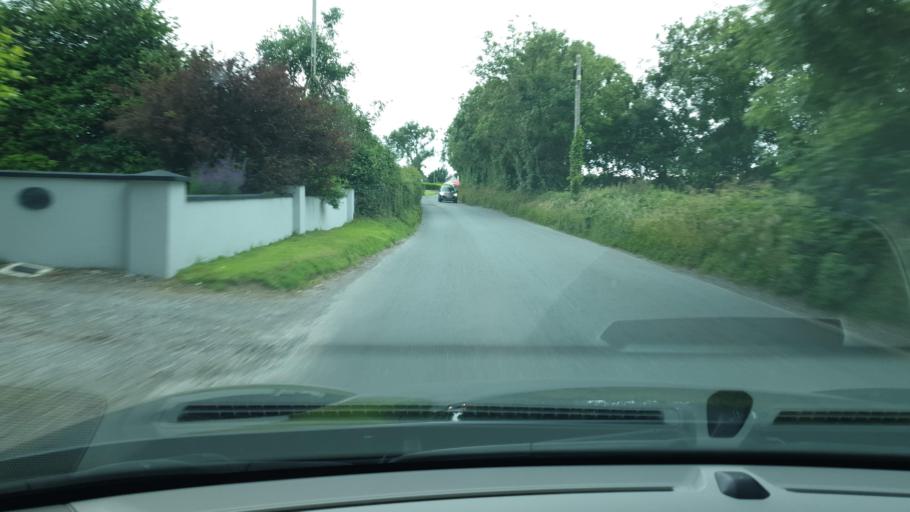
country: IE
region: Leinster
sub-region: An Mhi
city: Ratoath
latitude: 53.5389
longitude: -6.4383
